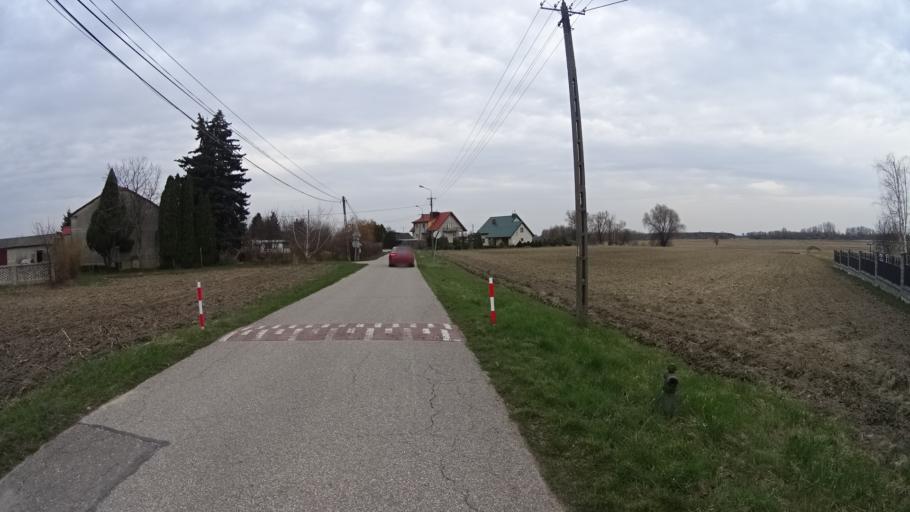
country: PL
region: Masovian Voivodeship
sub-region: Powiat warszawski zachodni
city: Jozefow
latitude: 52.2067
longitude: 20.6688
